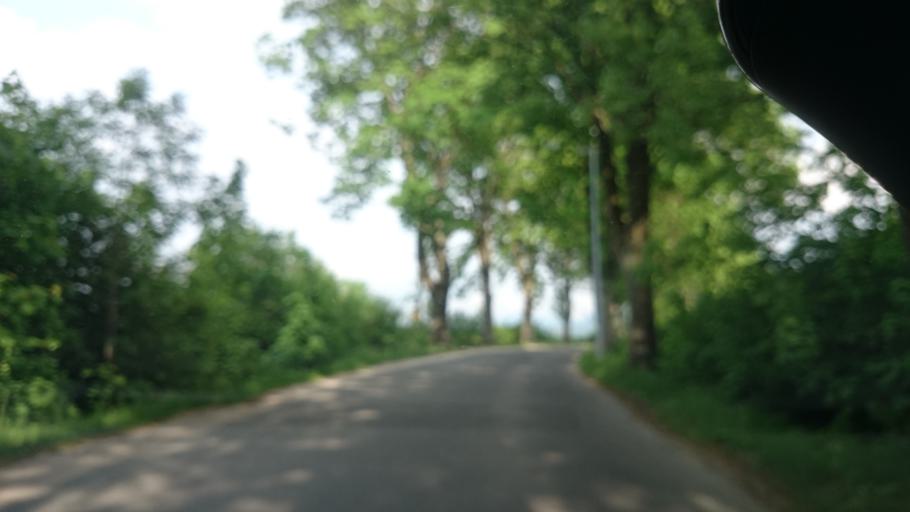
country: PL
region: Lower Silesian Voivodeship
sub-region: Powiat klodzki
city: Bystrzyca Klodzka
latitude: 50.2929
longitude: 16.6570
